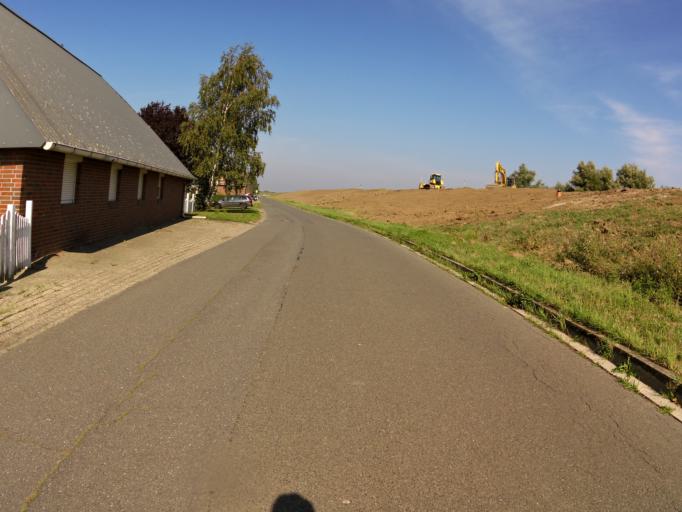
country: DE
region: Lower Saxony
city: Neuenkirchen
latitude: 53.2005
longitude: 8.4968
